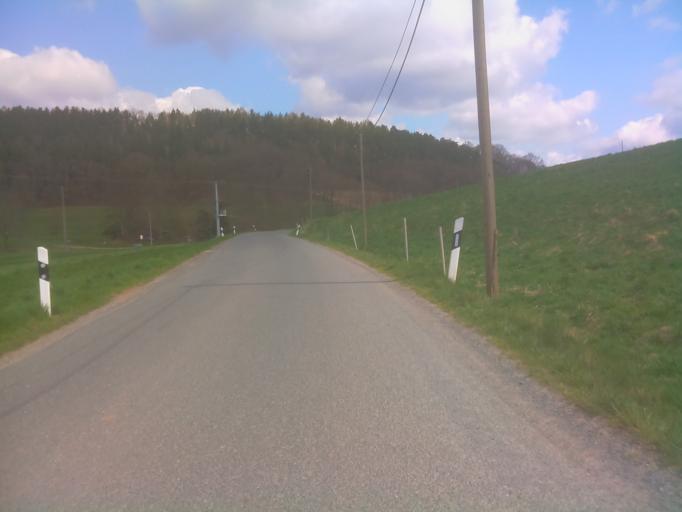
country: DE
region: Thuringia
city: Bremsnitz
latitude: 50.8032
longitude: 11.7785
